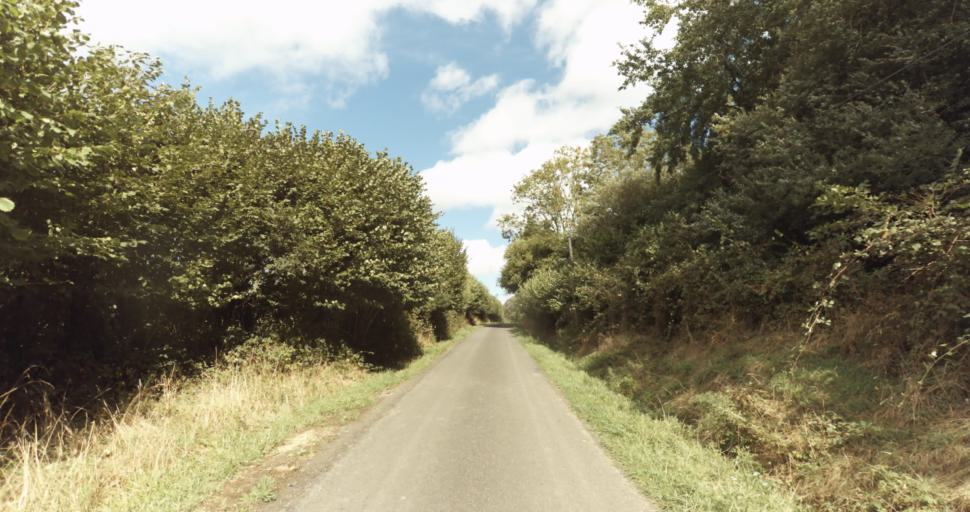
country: FR
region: Lower Normandy
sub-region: Departement de l'Orne
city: Gace
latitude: 48.7782
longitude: 0.3188
